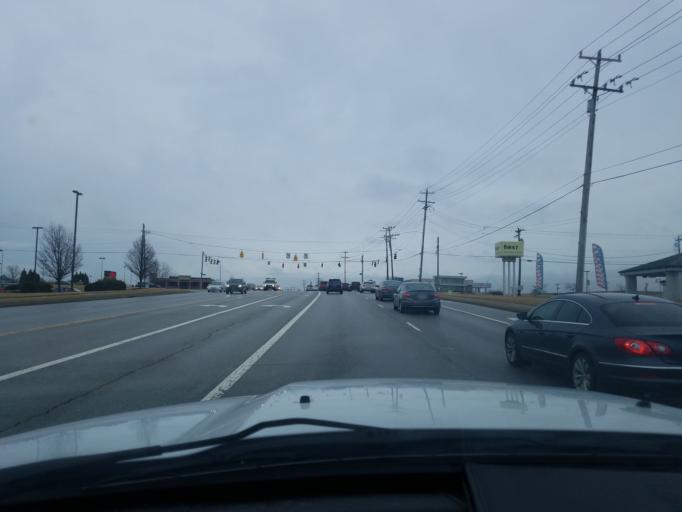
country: US
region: Ohio
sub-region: Butler County
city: Wetherington
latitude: 39.3532
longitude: -84.3657
